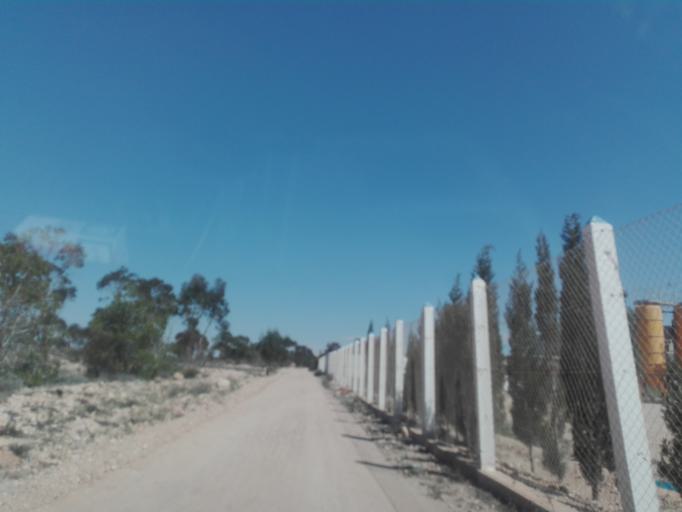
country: TN
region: Safaqis
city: Sfax
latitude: 34.7043
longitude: 10.5270
